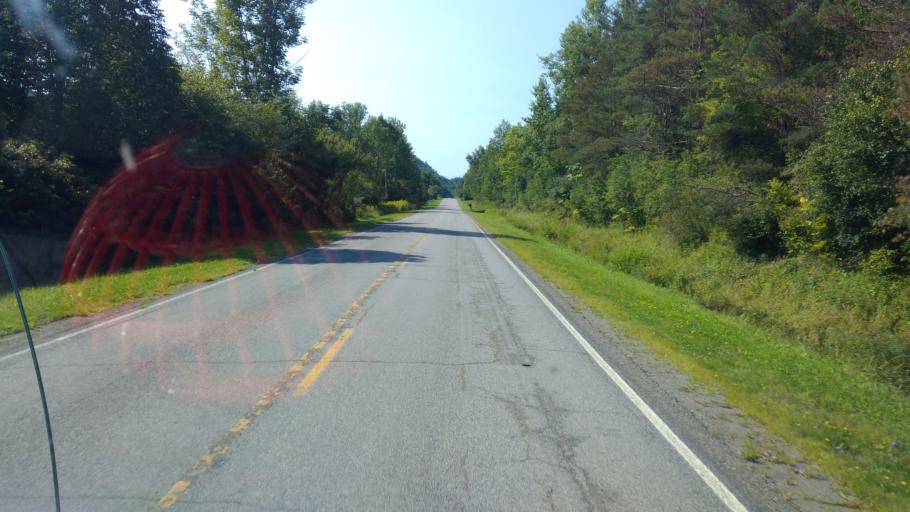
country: US
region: New York
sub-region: Allegany County
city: Bolivar
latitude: 42.1336
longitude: -78.1521
